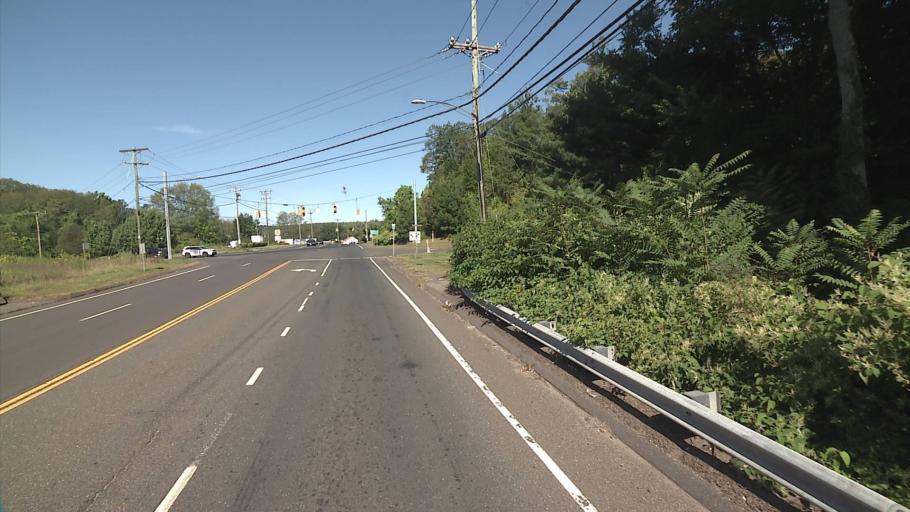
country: US
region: Connecticut
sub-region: New Haven County
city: Cheshire Village
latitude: 41.5146
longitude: -72.9240
